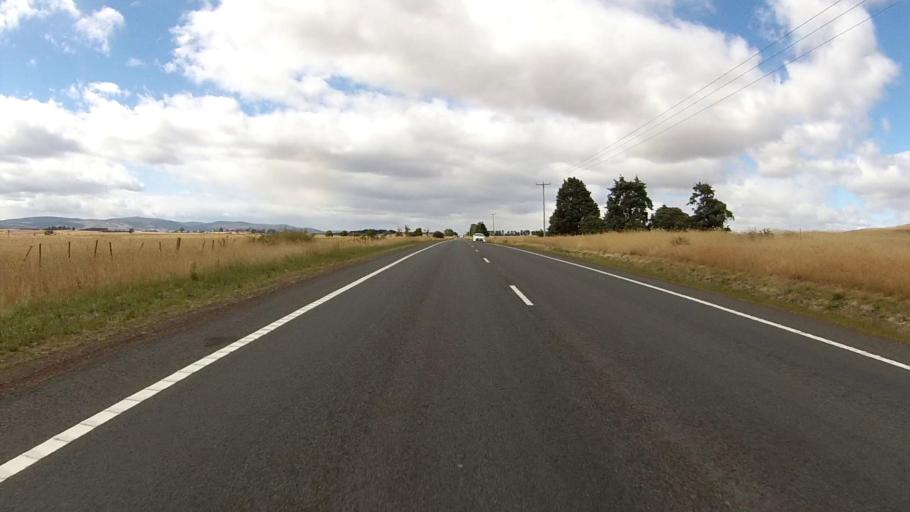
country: AU
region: Tasmania
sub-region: Northern Midlands
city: Evandale
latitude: -41.8962
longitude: 147.4736
